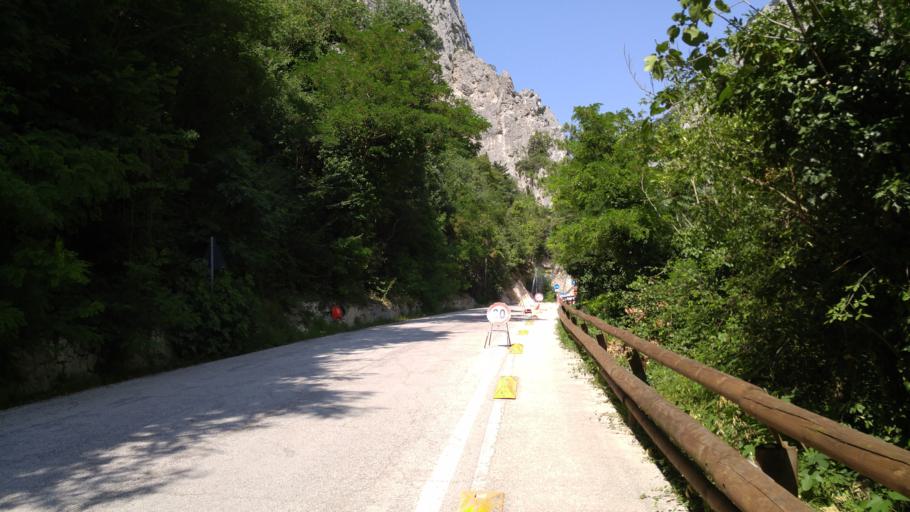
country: IT
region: The Marches
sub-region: Provincia di Pesaro e Urbino
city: Acqualagna
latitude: 43.6437
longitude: 12.7186
